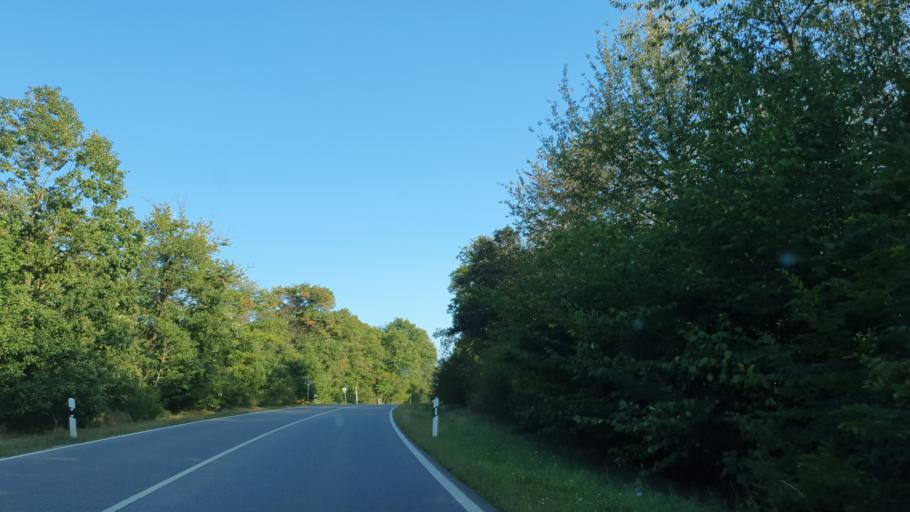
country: DE
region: Rheinland-Pfalz
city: Ney
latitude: 50.2180
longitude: 7.5378
